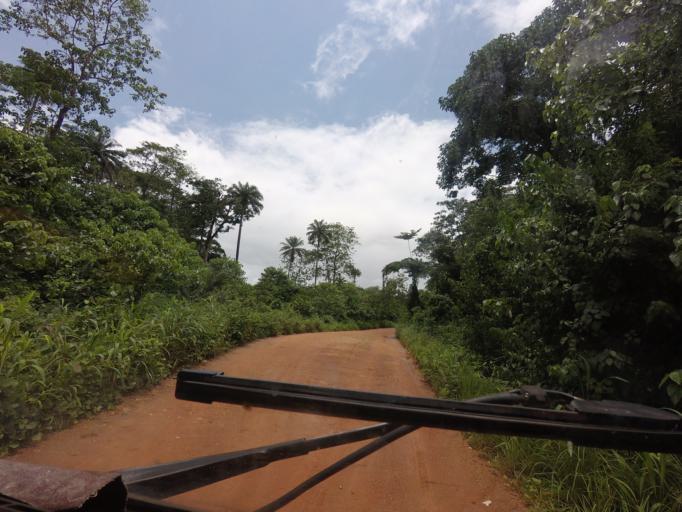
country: SL
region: Eastern Province
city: Pendembu
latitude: 8.1239
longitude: -10.6656
